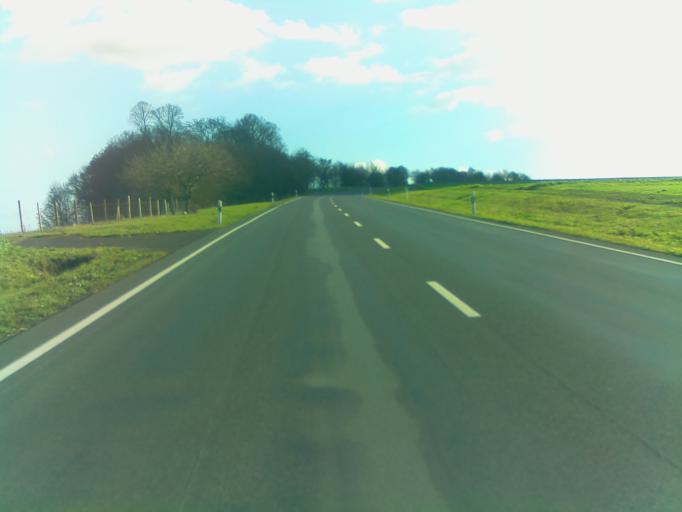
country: DE
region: Bavaria
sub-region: Regierungsbezirk Unterfranken
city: Saal an der Saale
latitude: 50.3138
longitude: 10.3712
